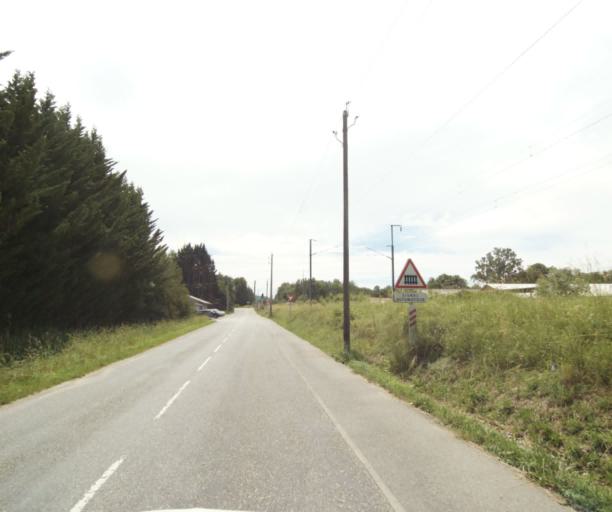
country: FR
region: Rhone-Alpes
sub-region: Departement de la Haute-Savoie
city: Perrignier
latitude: 46.3008
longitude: 6.4216
